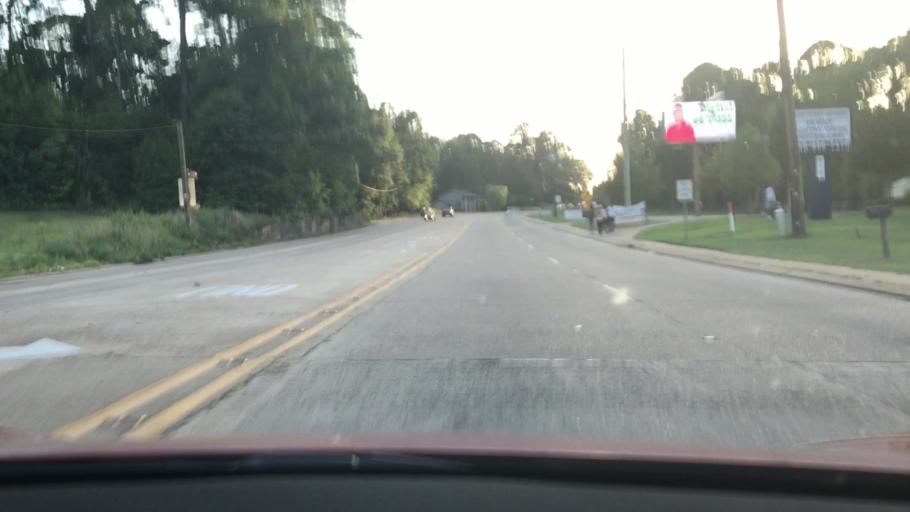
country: US
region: Louisiana
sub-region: Bossier Parish
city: Bossier City
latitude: 32.4016
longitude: -93.7811
